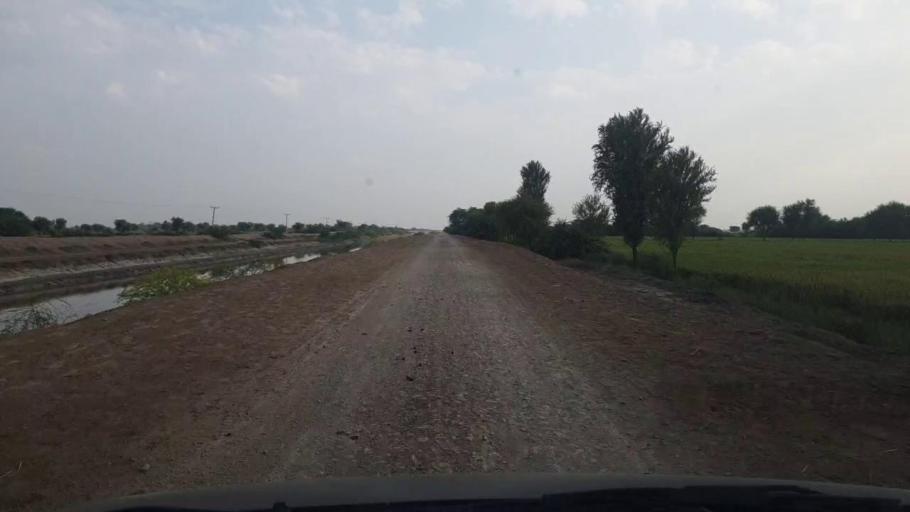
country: PK
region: Sindh
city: Badin
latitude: 24.5207
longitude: 68.6823
